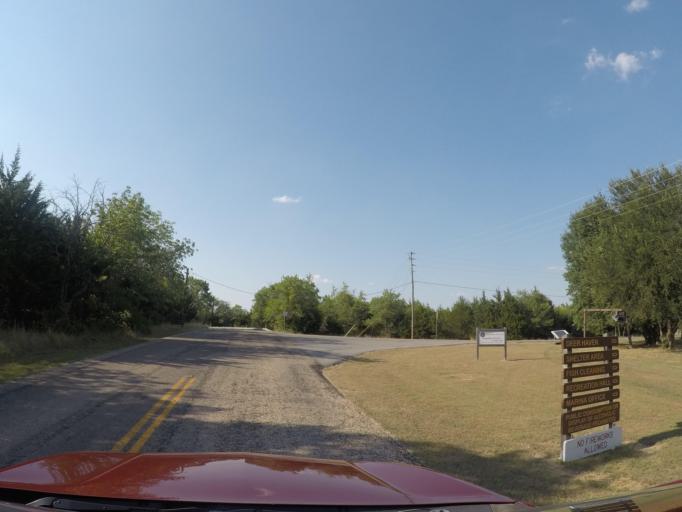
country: US
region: Texas
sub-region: Grayson County
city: Preston
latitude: 33.8218
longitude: -96.6140
